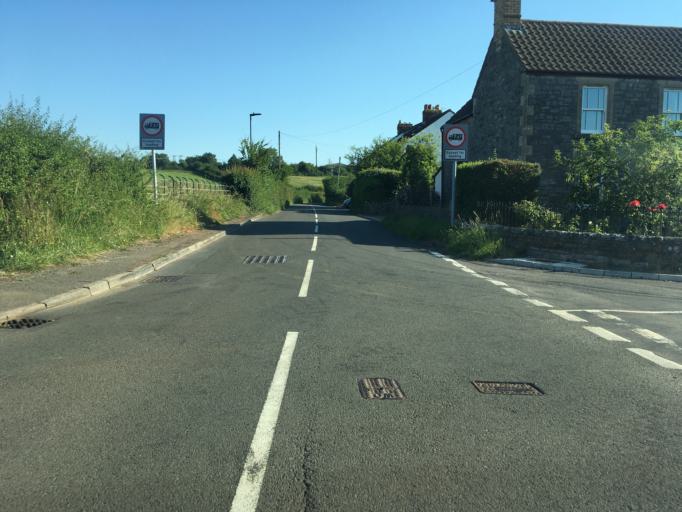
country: GB
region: England
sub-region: South Gloucestershire
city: Siston
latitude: 51.4595
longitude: -2.4287
